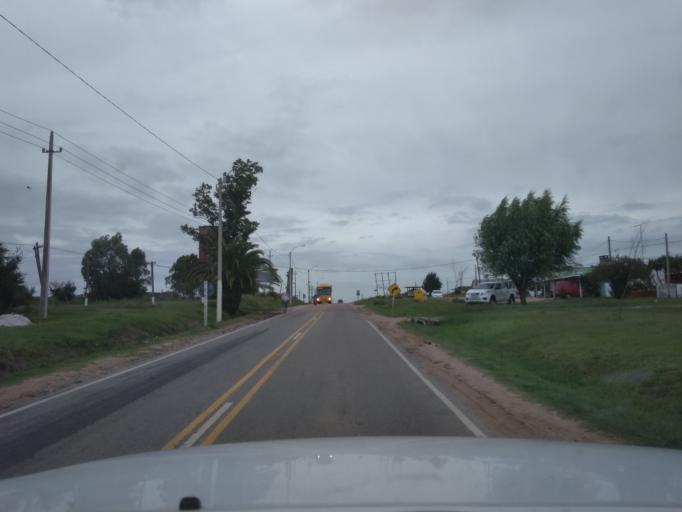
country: UY
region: Canelones
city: Tala
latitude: -34.3493
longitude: -55.7670
